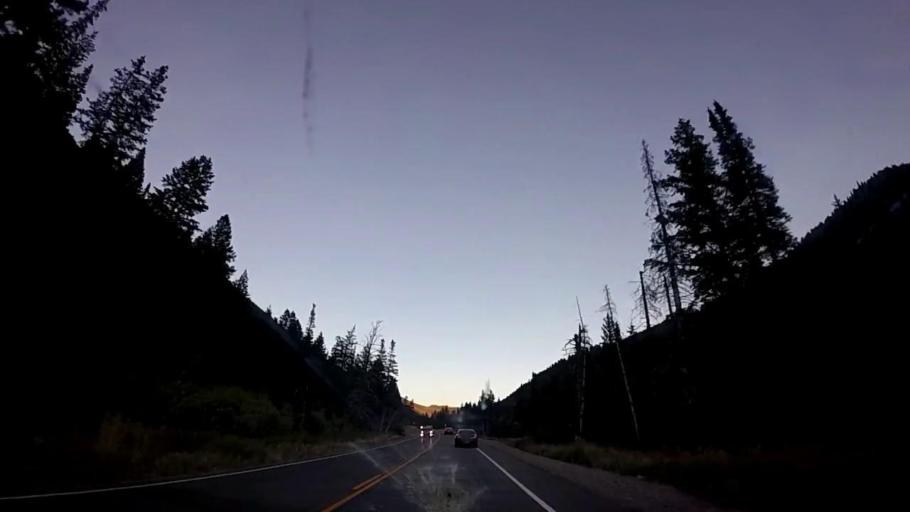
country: US
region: Utah
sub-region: Summit County
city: Snyderville
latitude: 40.6408
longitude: -111.6317
